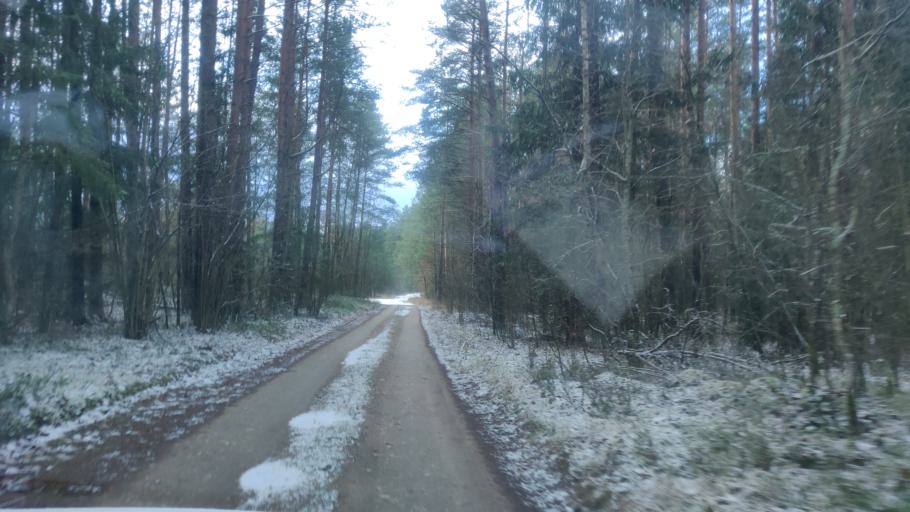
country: LT
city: Trakai
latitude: 54.5634
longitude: 24.9155
